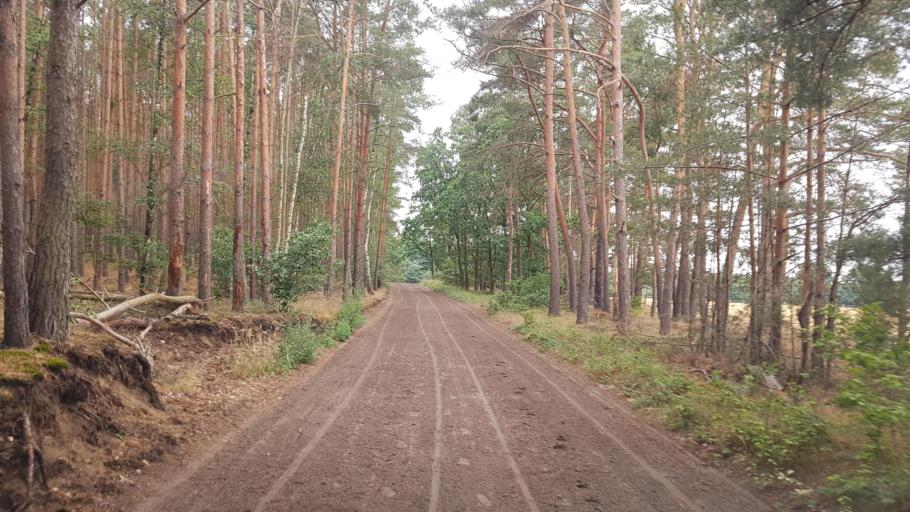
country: DE
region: Brandenburg
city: Trebbin
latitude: 52.2520
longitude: 13.1672
